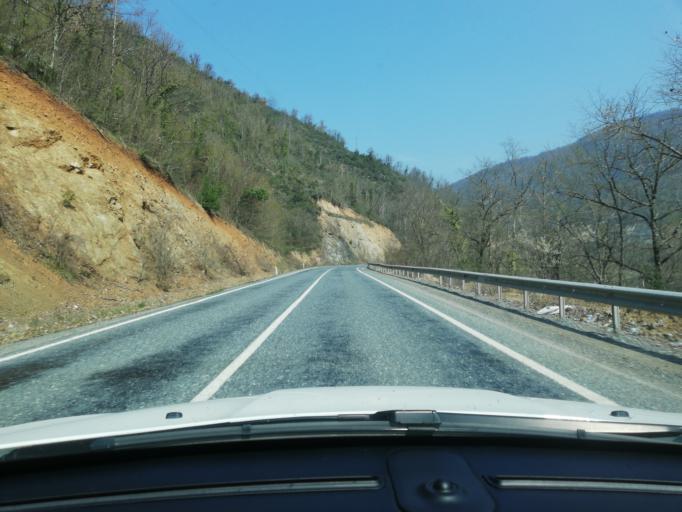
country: TR
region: Zonguldak
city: Gokcebey
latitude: 41.2487
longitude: 32.1676
